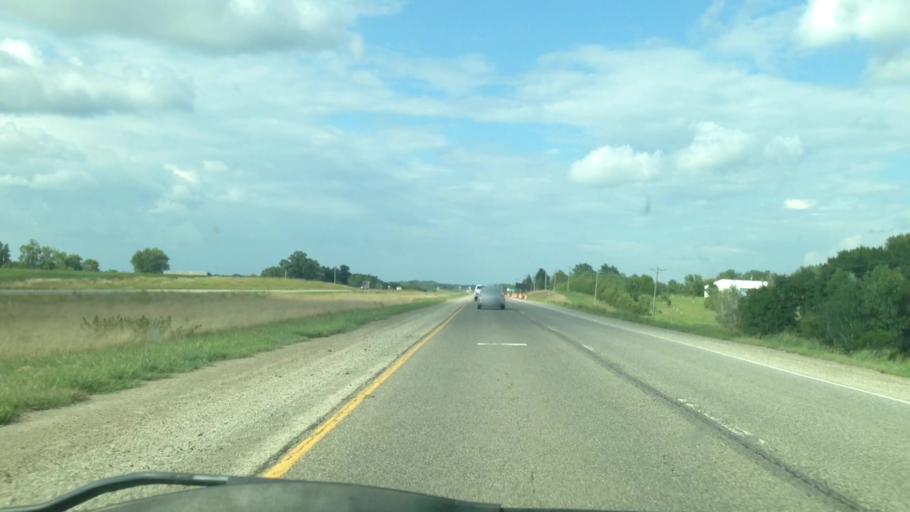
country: US
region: Iowa
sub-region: Henry County
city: Mount Pleasant
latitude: 40.8819
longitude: -91.5630
